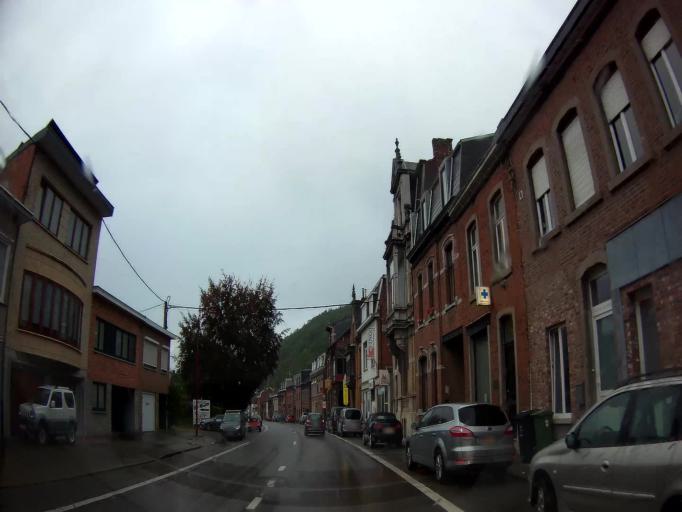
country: BE
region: Wallonia
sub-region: Province de Liege
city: Trooz
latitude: 50.5755
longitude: 5.6867
